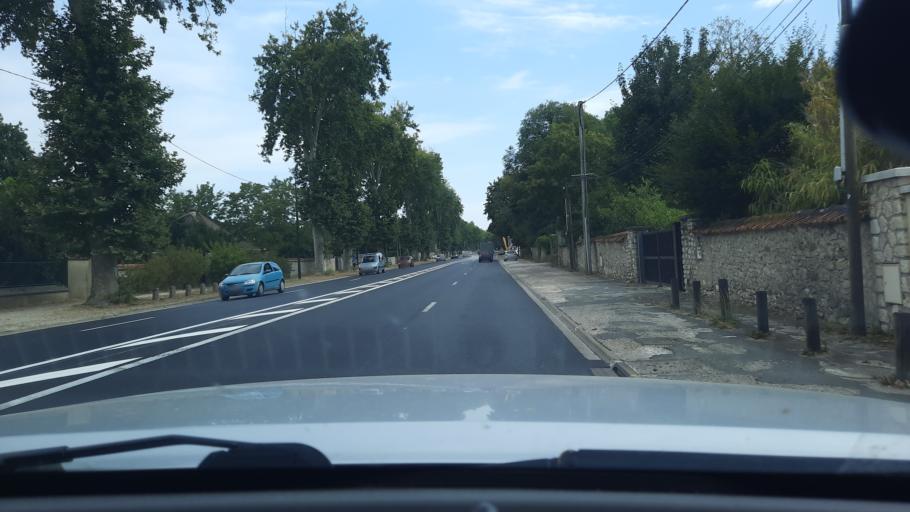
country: FR
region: Ile-de-France
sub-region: Departement de Seine-et-Marne
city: Dammarie-les-Lys
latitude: 48.5206
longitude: 2.6541
